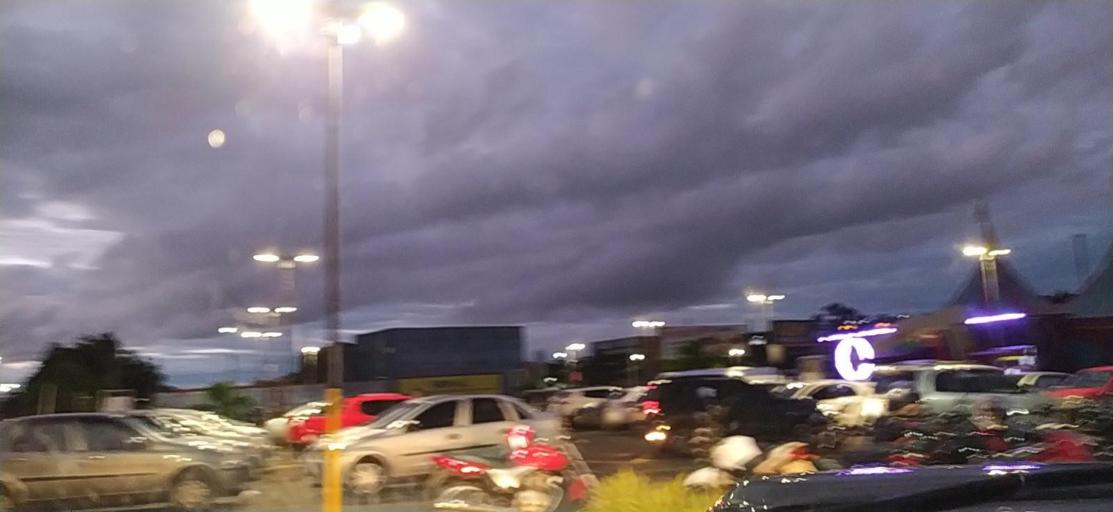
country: BR
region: Sao Paulo
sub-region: Hortolandia
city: Hortolandia
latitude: -22.8626
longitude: -47.2131
